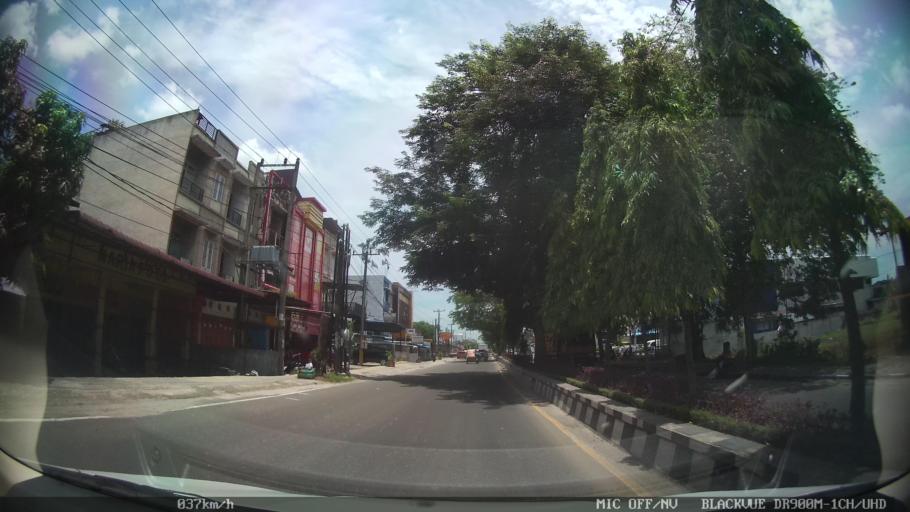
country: ID
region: North Sumatra
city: Percut
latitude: 3.5540
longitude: 98.8712
